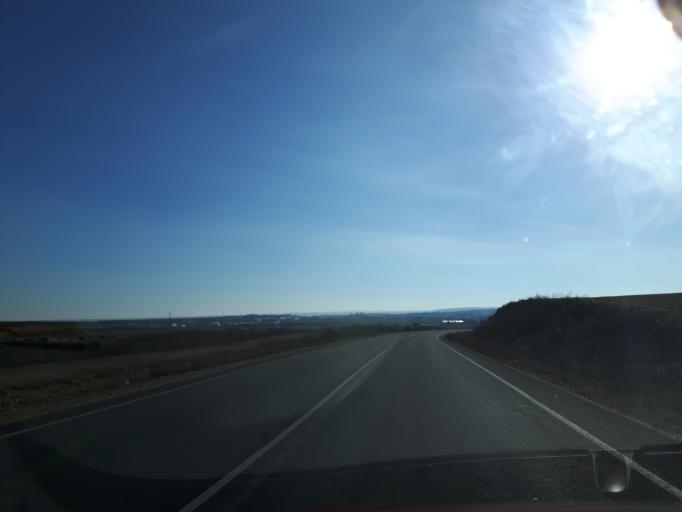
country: ES
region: Castille and Leon
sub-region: Provincia de Salamanca
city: Monterrubio de Armuna
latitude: 41.0164
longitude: -5.6325
